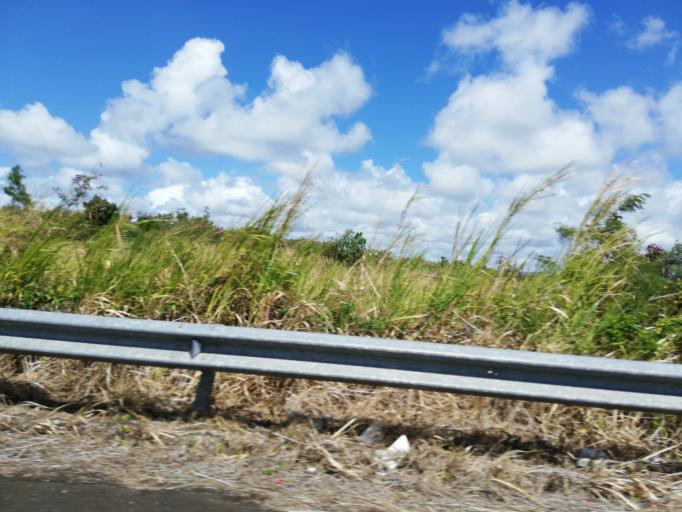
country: MU
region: Riviere du Rempart
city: Goodlands
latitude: -20.0514
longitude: 57.6568
